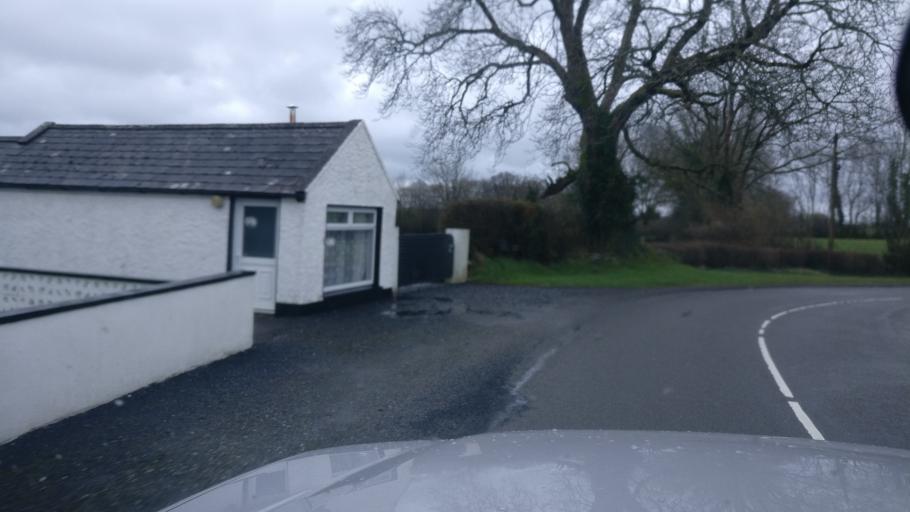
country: IE
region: Connaught
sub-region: County Galway
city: Ballinasloe
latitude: 53.2635
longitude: -8.3572
